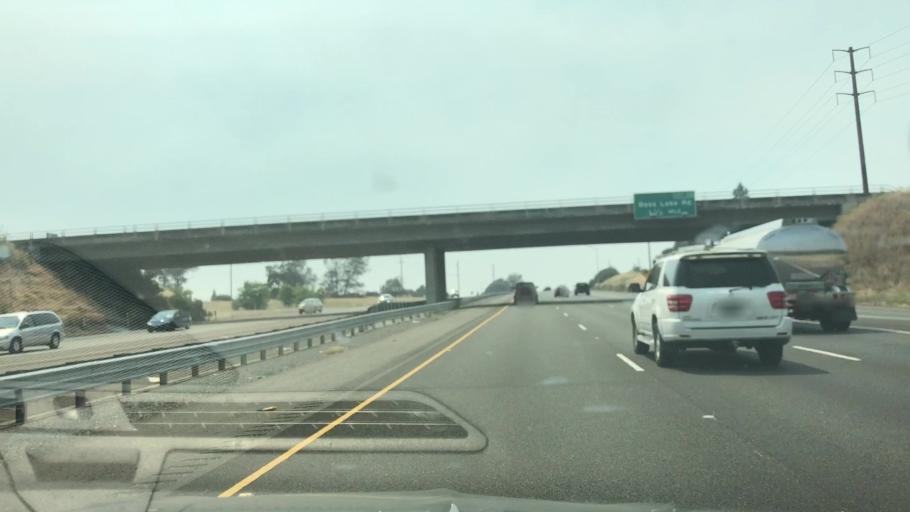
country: US
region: California
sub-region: El Dorado County
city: Cameron Park
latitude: 38.6568
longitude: -120.9975
